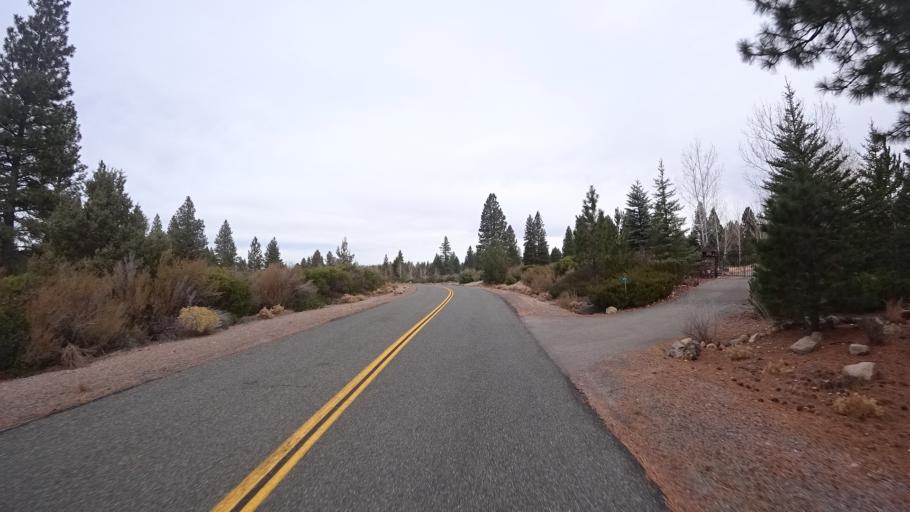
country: US
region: California
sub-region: Siskiyou County
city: Weed
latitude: 41.4110
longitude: -122.3648
